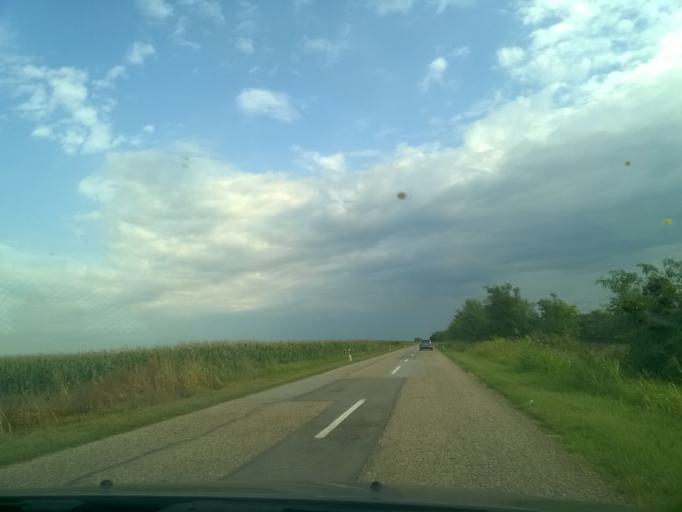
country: RS
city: Uzdin
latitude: 45.1628
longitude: 20.6172
